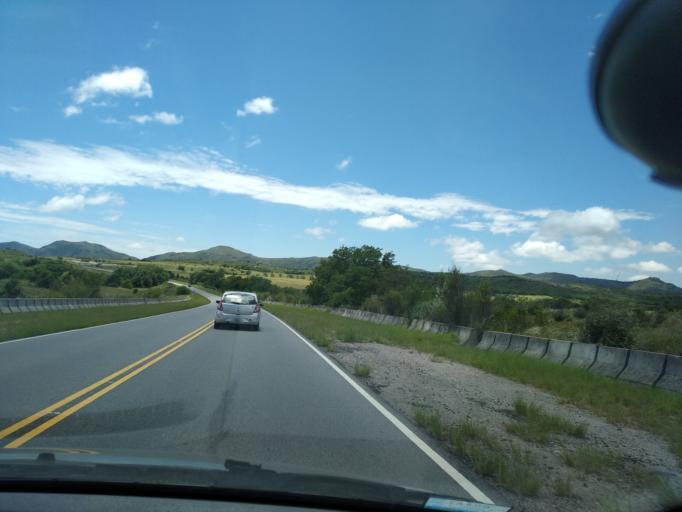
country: AR
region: Cordoba
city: Cuesta Blanca
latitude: -31.5762
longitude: -64.5980
